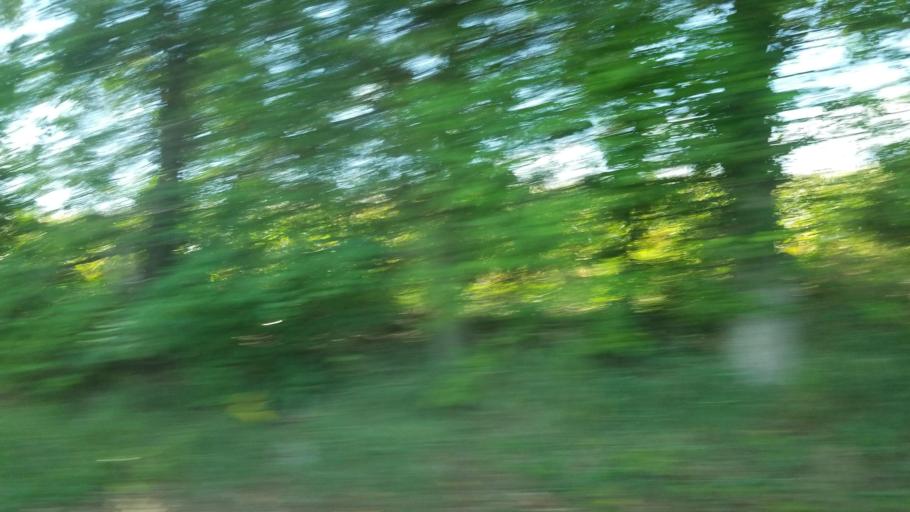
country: US
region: Illinois
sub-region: Williamson County
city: Johnston City
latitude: 37.7877
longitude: -88.8175
